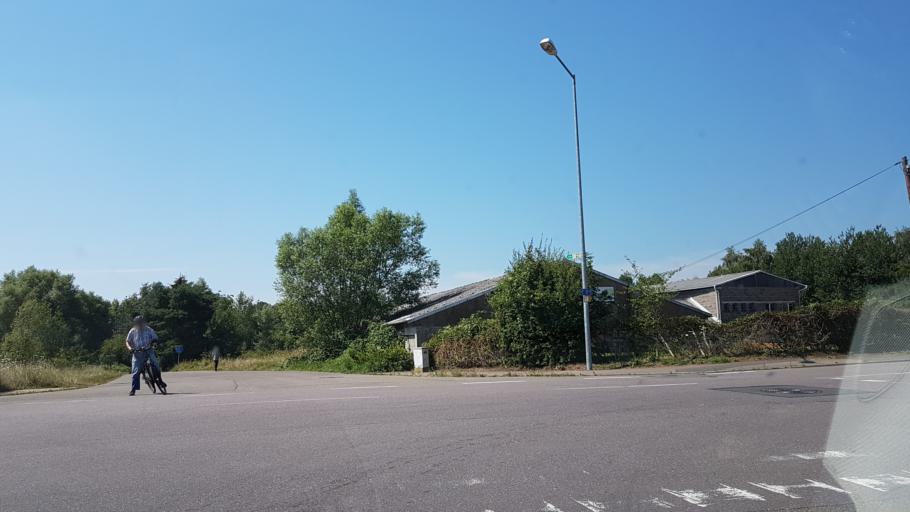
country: DE
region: Saarland
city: Homburg
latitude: 49.3131
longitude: 7.3294
